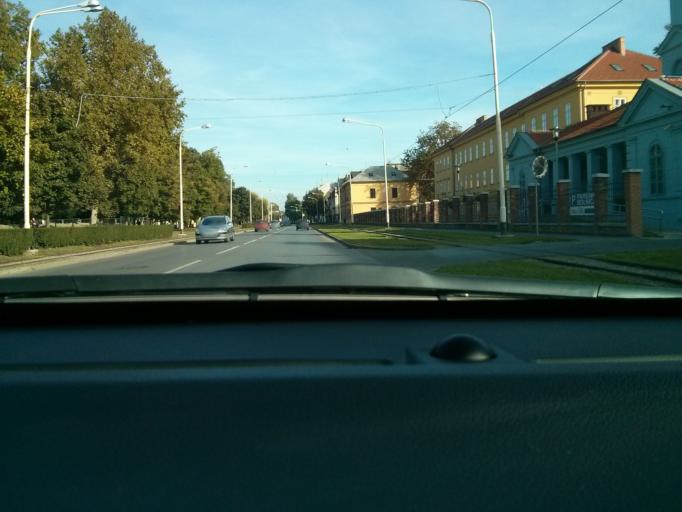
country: HR
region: Osjecko-Baranjska
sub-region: Grad Osijek
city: Osijek
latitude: 45.5568
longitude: 18.7124
